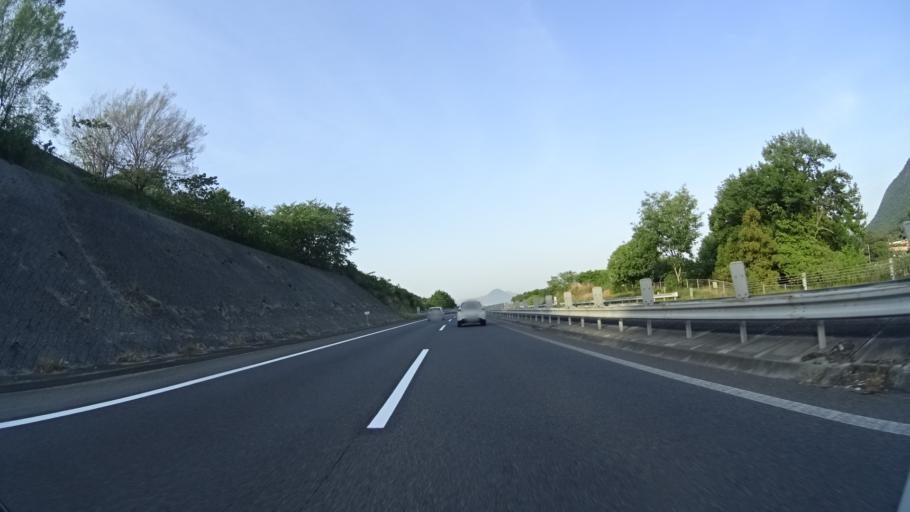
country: JP
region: Kagawa
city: Tadotsu
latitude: 34.2259
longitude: 133.7354
